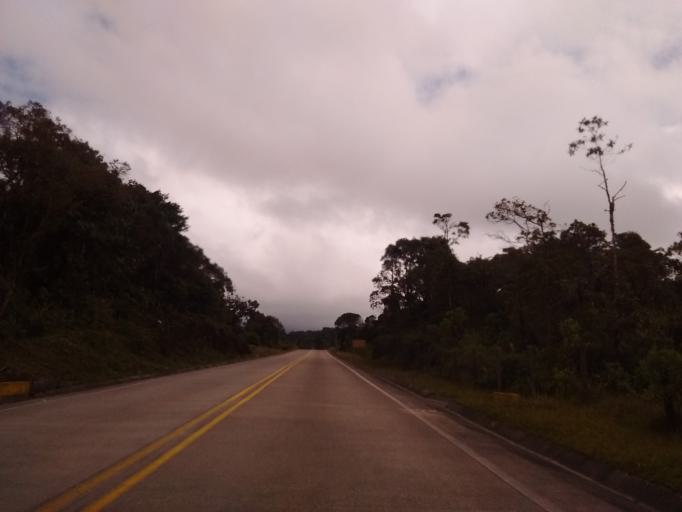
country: CO
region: Huila
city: Isnos
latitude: 2.0545
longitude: -76.3217
